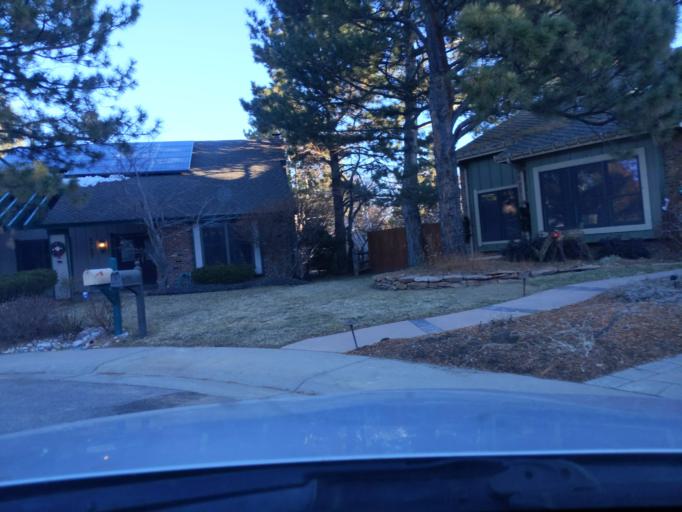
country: US
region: Colorado
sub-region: Arapahoe County
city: Centennial
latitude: 39.5764
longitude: -104.8864
